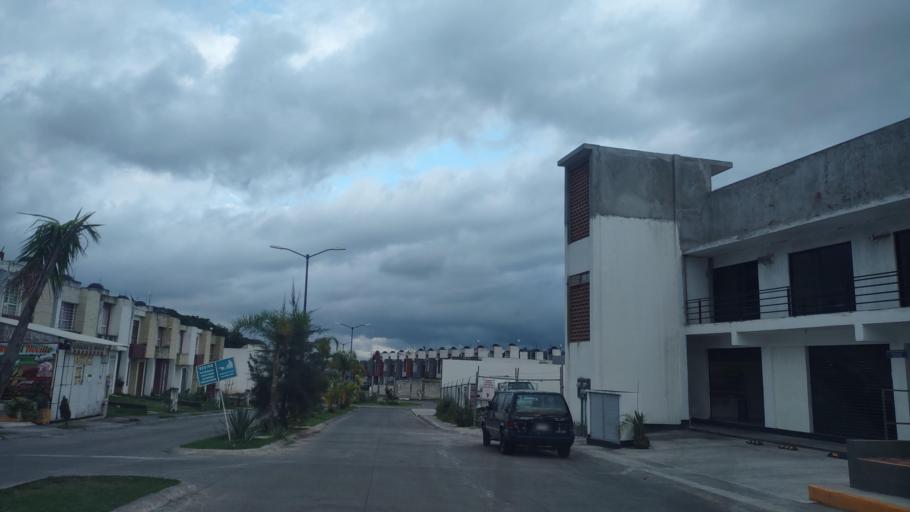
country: MX
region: Veracruz
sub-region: Ixtaczoquitlan
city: Buenavista
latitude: 18.8830
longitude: -97.0605
